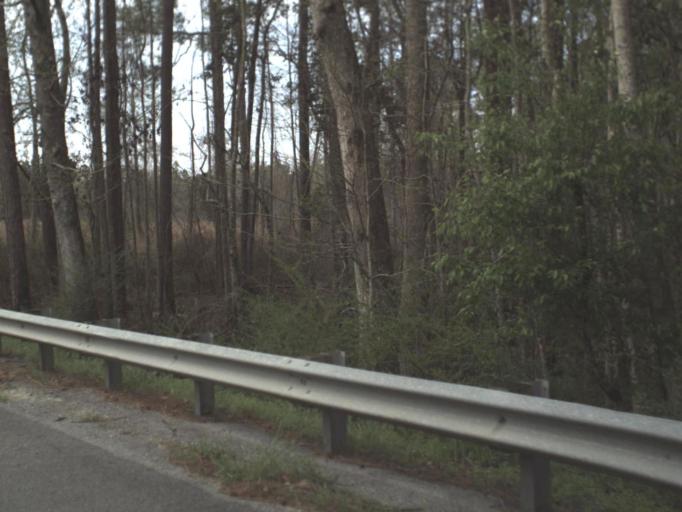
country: US
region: Florida
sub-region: Holmes County
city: Bonifay
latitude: 30.8298
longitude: -85.6674
